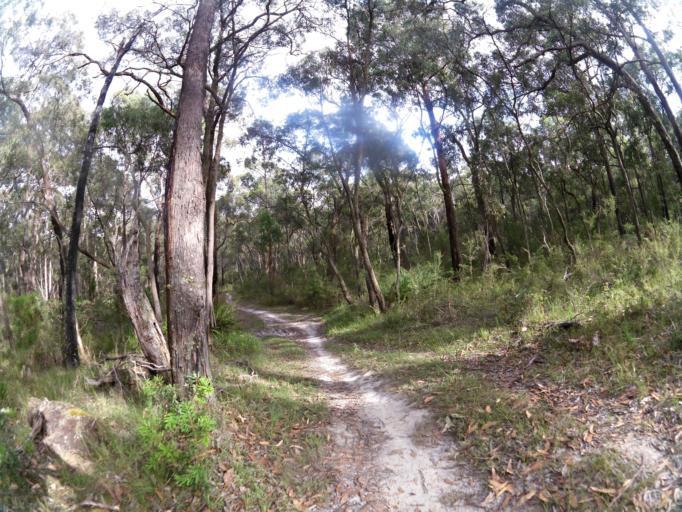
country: AU
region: Victoria
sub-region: Colac-Otway
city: Colac
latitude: -38.4862
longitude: 143.7072
